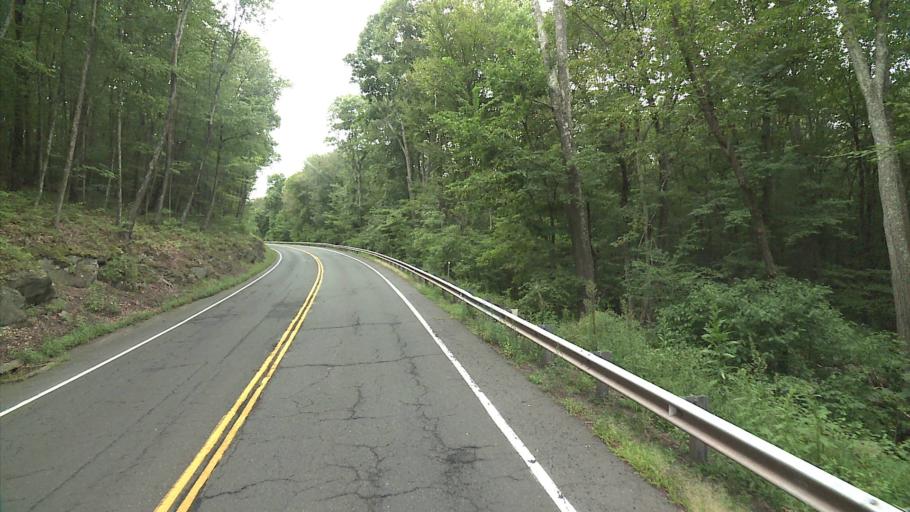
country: US
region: Connecticut
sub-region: Hartford County
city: Manchester
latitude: 41.7696
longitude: -72.4645
